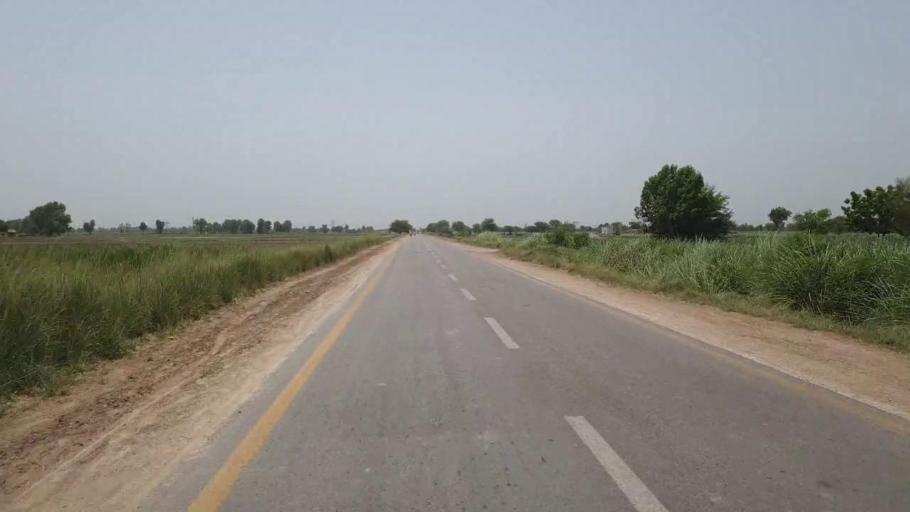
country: PK
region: Sindh
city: Moro
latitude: 26.6054
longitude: 68.0524
